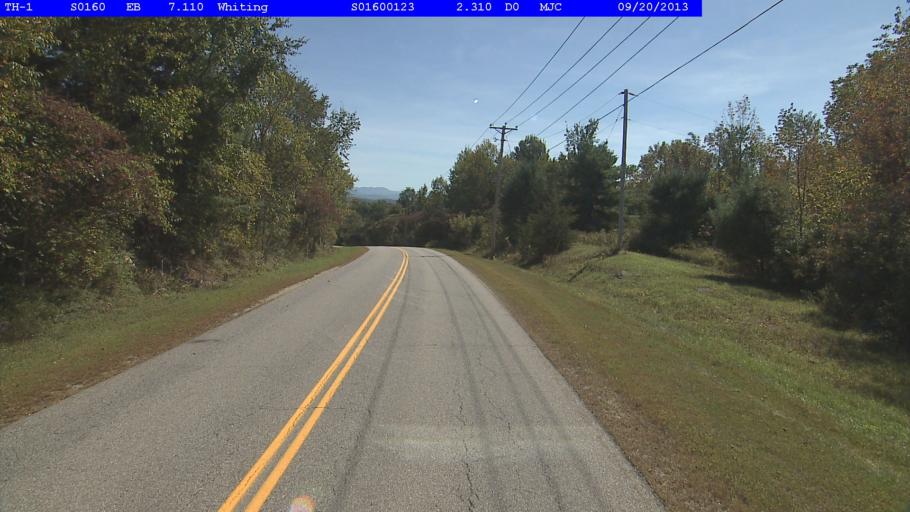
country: US
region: Vermont
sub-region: Rutland County
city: Brandon
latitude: 43.8559
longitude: -73.1836
